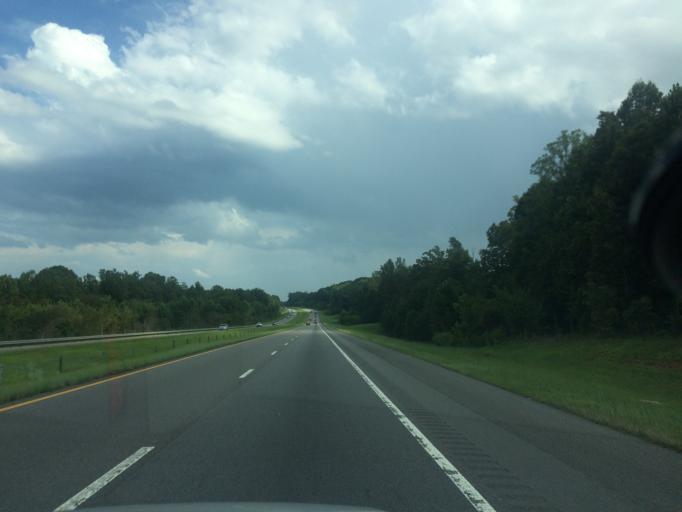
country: US
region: North Carolina
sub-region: Catawba County
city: Mountain View
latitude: 35.6697
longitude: -81.3324
